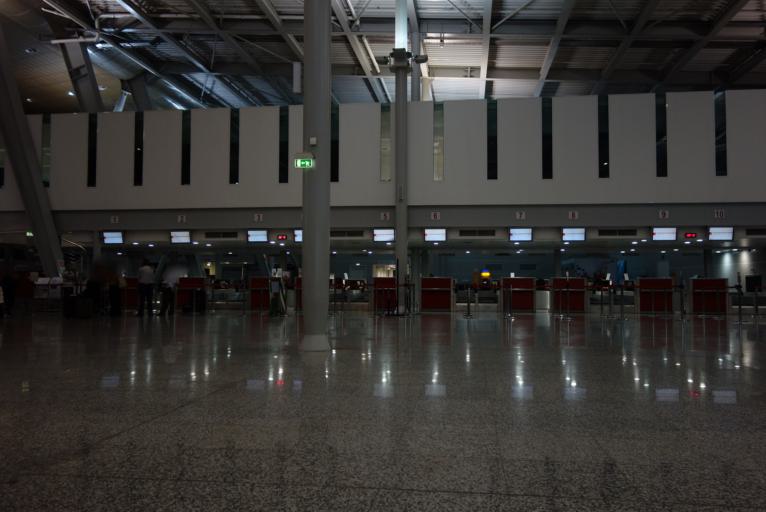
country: AL
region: Tirane
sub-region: Rrethi i Tiranes
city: Preze
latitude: 41.4192
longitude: 19.7132
